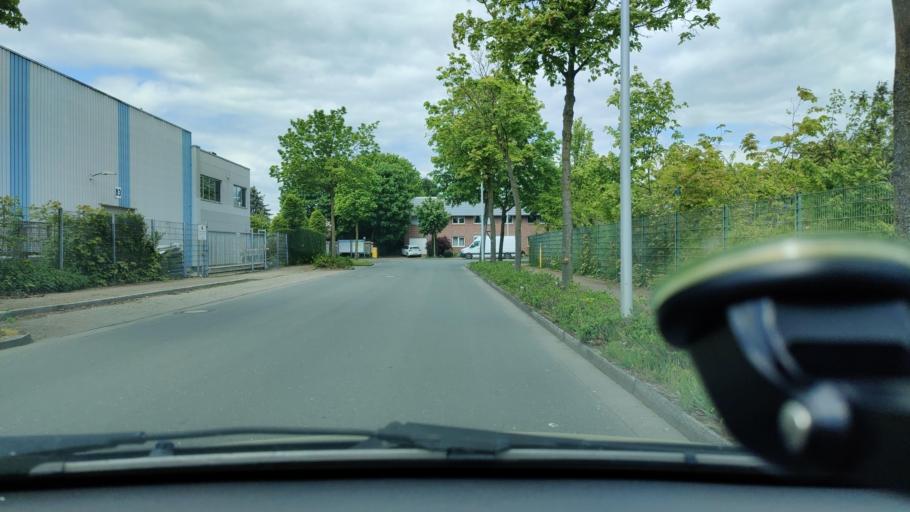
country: DE
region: North Rhine-Westphalia
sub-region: Regierungsbezirk Dusseldorf
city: Bocholt
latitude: 51.8145
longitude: 6.5663
